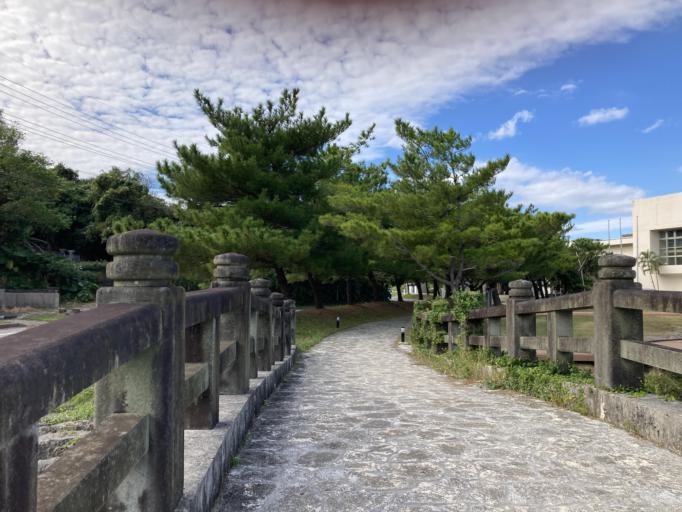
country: JP
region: Okinawa
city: Ishikawa
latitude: 26.4357
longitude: 127.7940
